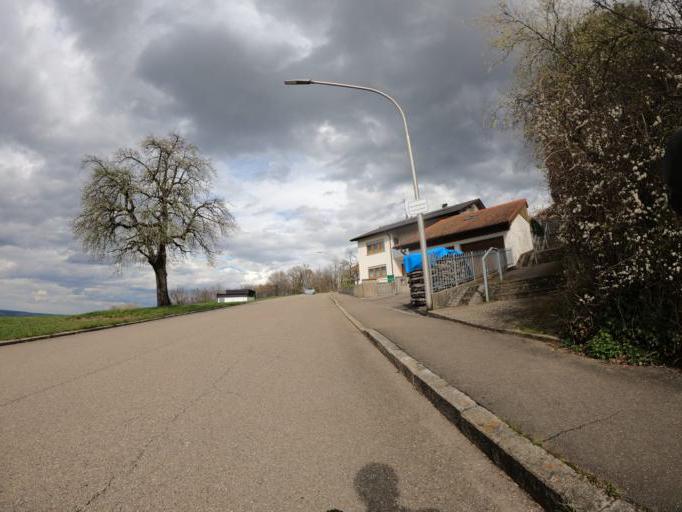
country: DE
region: Baden-Wuerttemberg
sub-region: Tuebingen Region
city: Gomaringen
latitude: 48.4203
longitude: 9.1143
